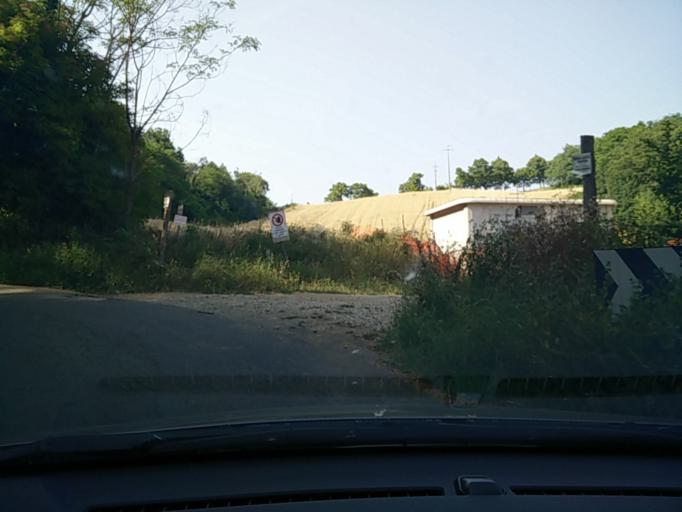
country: IT
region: Lombardy
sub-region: Provincia di Pavia
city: Susella
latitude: 44.9174
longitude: 9.1001
